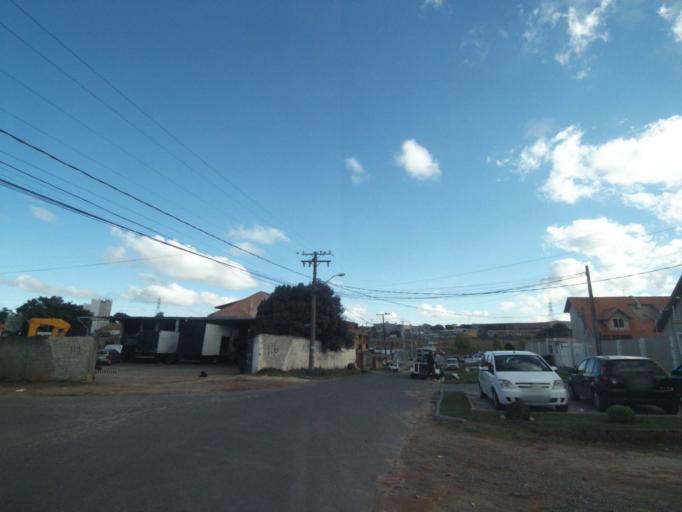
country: BR
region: Parana
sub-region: Sao Jose Dos Pinhais
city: Sao Jose dos Pinhais
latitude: -25.5247
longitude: -49.2910
